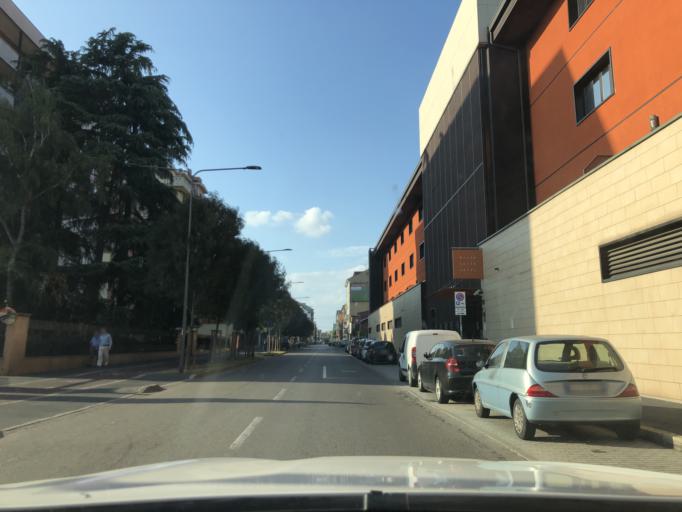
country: IT
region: Lombardy
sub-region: Citta metropolitana di Milano
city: Novate Milanese
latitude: 45.5000
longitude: 9.1427
